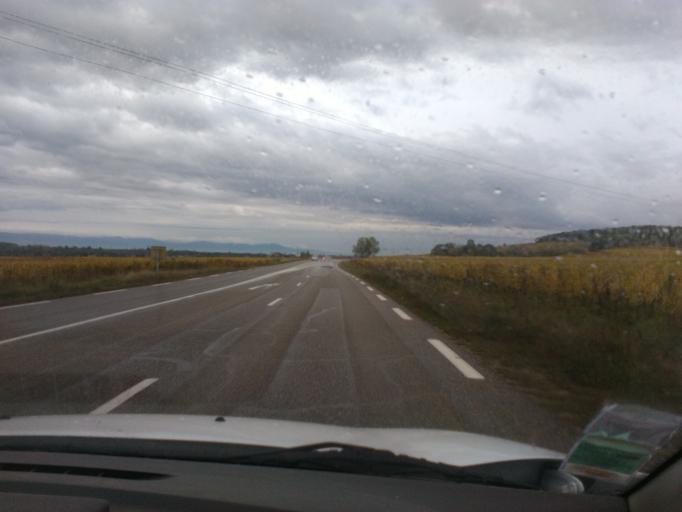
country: FR
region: Alsace
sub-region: Departement du Haut-Rhin
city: Ammerschwihr
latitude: 48.1152
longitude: 7.2905
